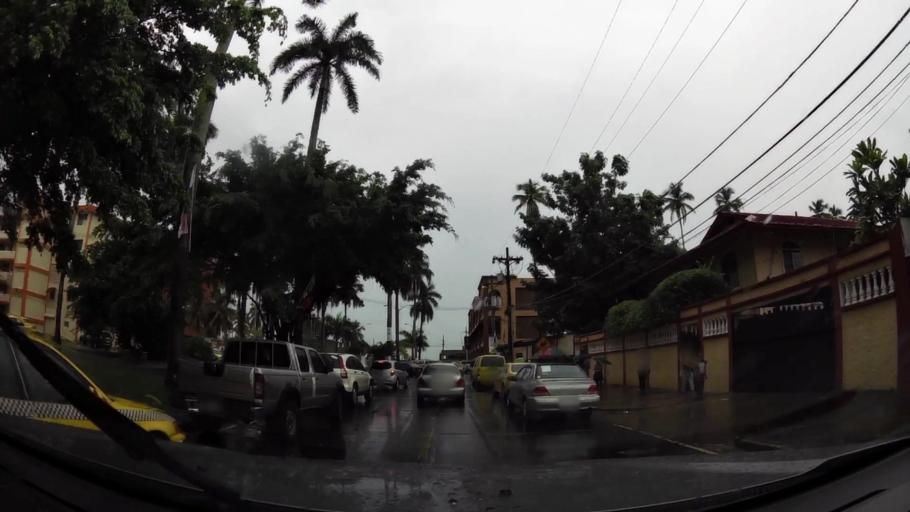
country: PA
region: Colon
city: Colon
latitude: 9.3651
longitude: -79.9037
